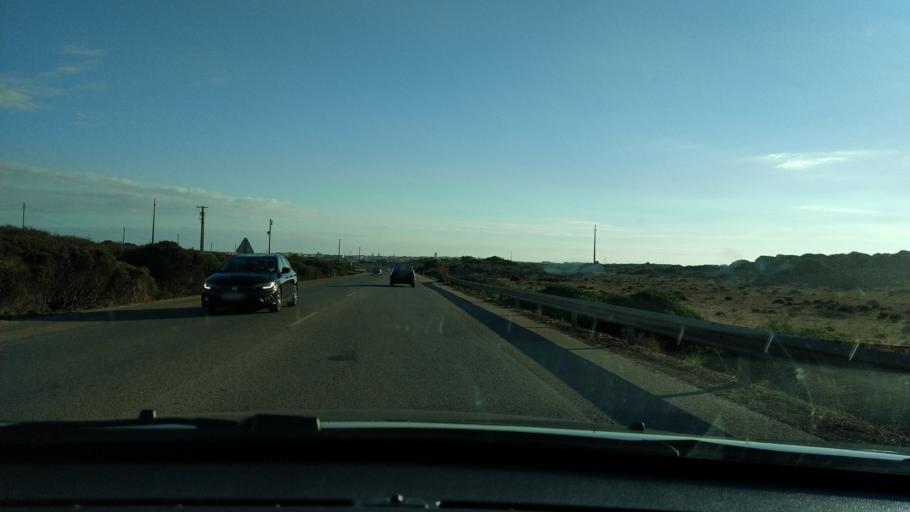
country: PT
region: Faro
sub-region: Vila do Bispo
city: Sagres
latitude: 37.0286
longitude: -8.9367
